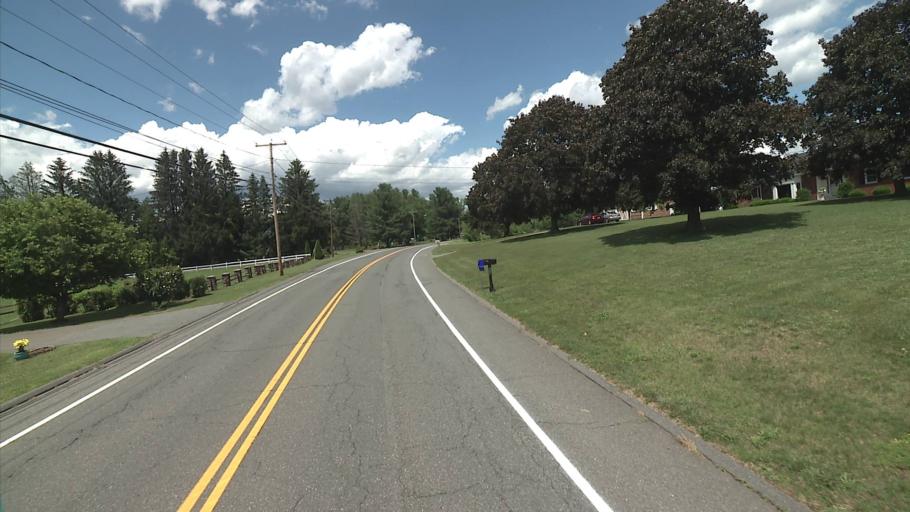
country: US
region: Connecticut
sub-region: Tolland County
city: Somers
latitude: 42.0019
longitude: -72.4887
